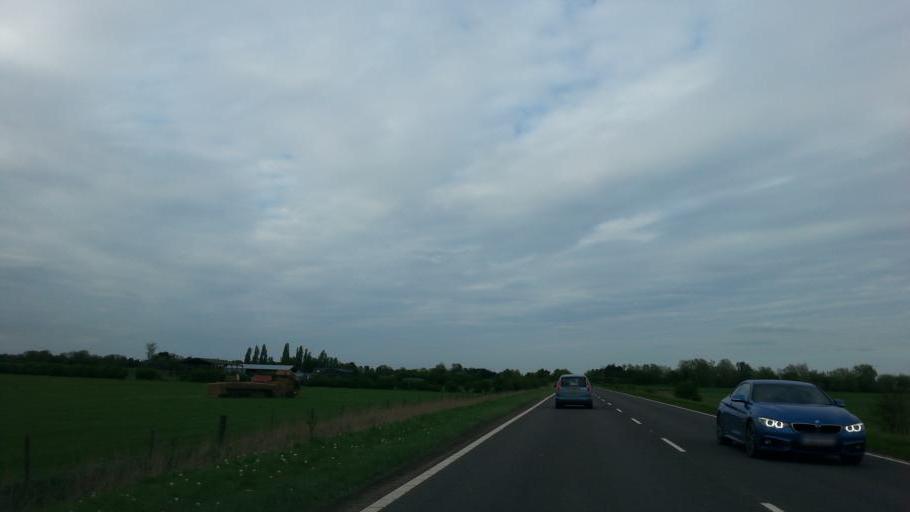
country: GB
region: England
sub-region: Cambridgeshire
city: Doddington
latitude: 52.4865
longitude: 0.0647
